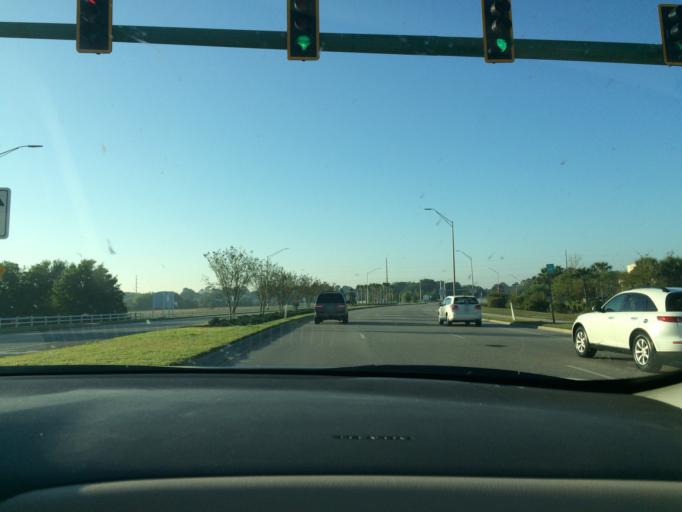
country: US
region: Florida
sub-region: Sarasota County
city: The Meadows
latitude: 27.4359
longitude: -82.4288
